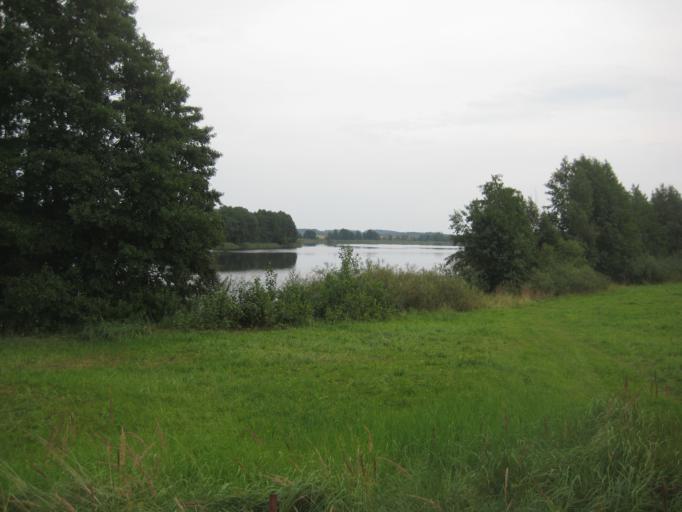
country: LT
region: Panevezys
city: Rokiskis
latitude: 55.7390
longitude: 25.5202
